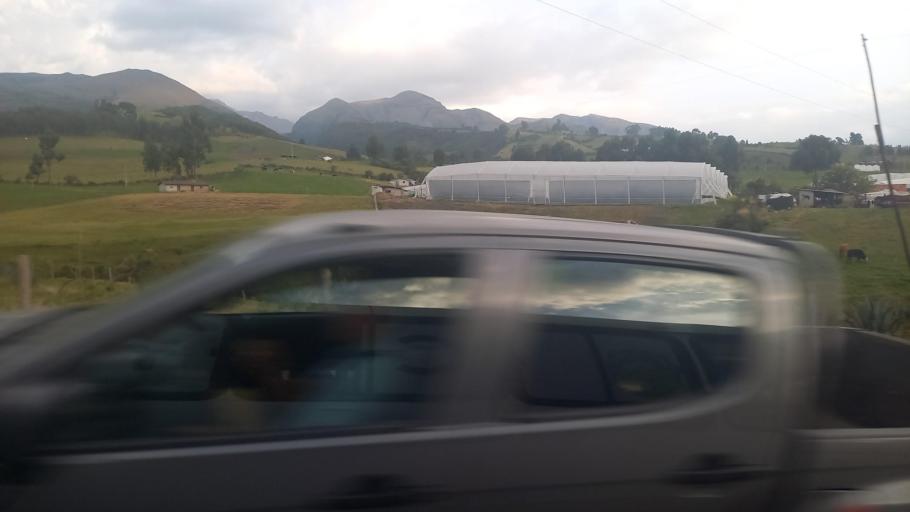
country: EC
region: Pichincha
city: Cayambe
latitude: 0.0960
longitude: -78.0901
